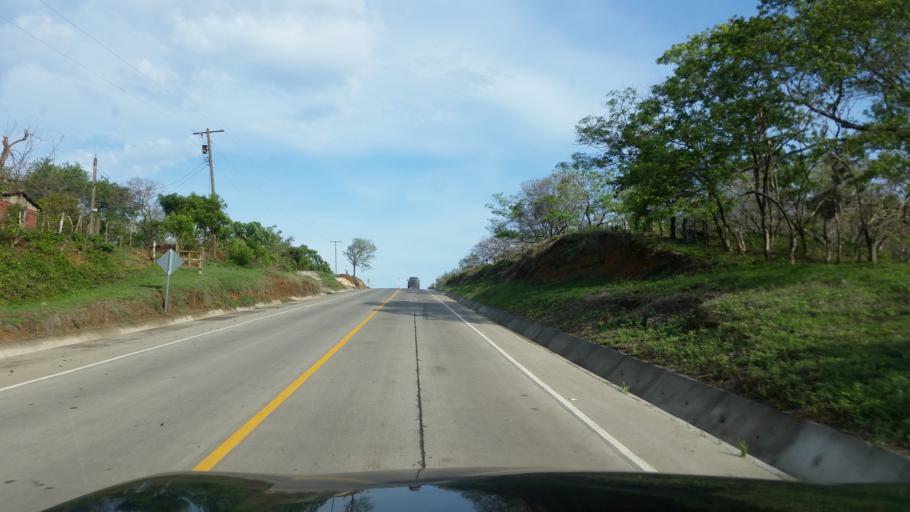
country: NI
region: Leon
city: Nagarote
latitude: 12.1145
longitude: -86.6095
